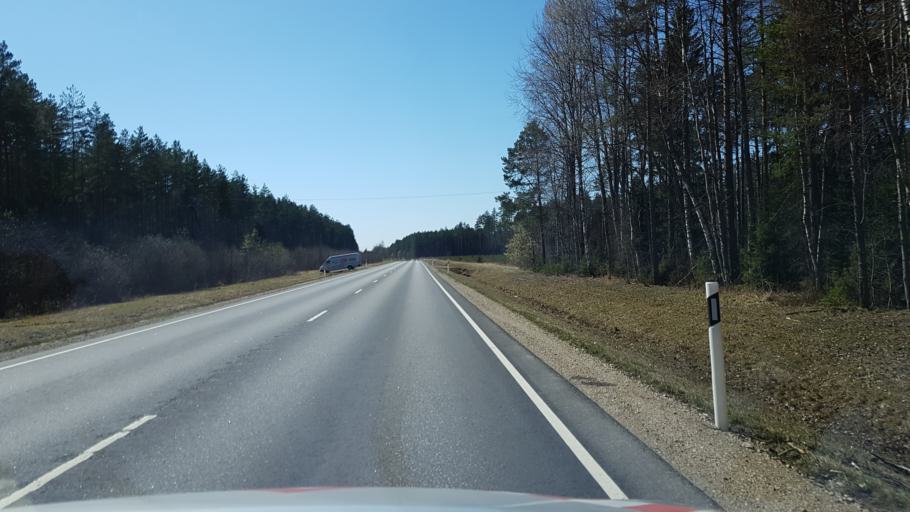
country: EE
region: Jogevamaa
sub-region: Mustvee linn
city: Mustvee
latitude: 58.9680
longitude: 27.1105
